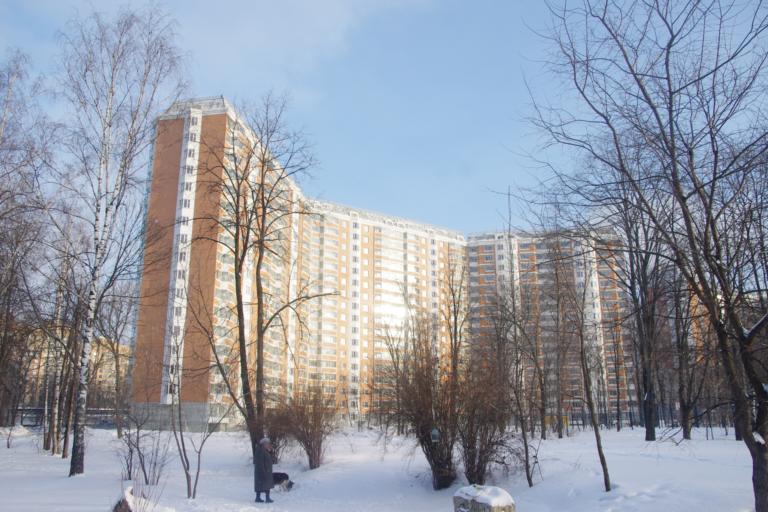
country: RU
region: Moscow
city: Leonovo
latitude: 55.8552
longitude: 37.6421
